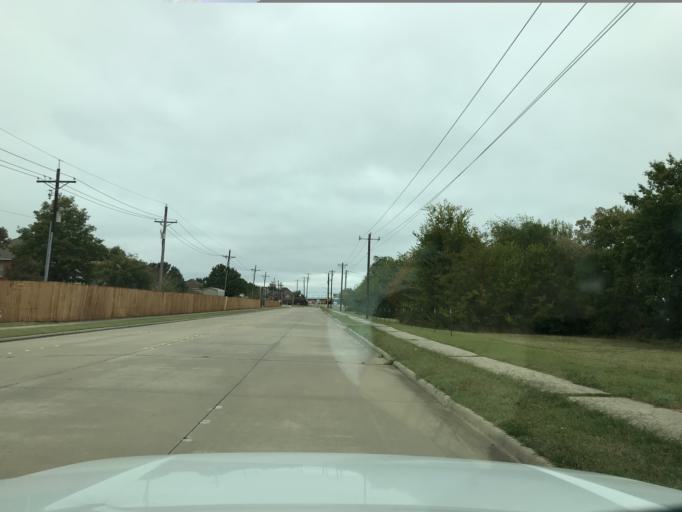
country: US
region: Texas
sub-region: Denton County
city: Highland Village
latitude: 33.0784
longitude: -97.0270
